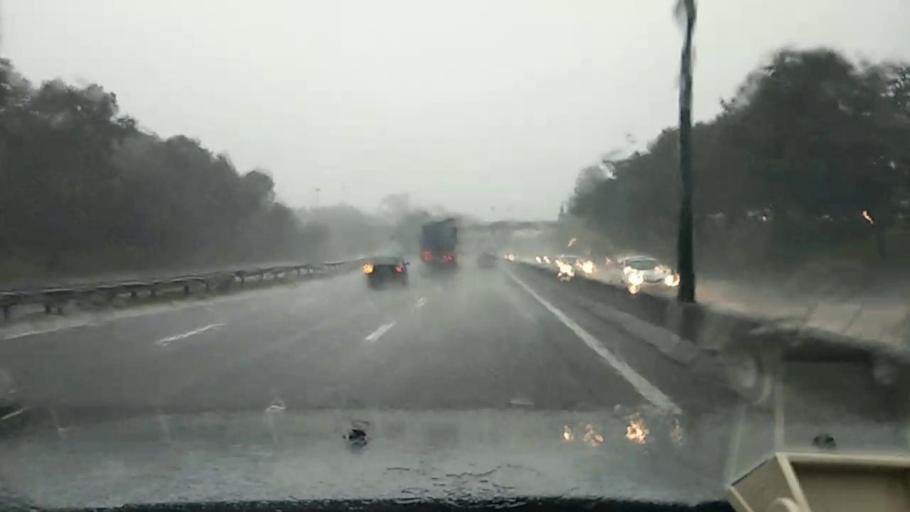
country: MY
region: Selangor
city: Kampong Baharu Balakong
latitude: 2.9818
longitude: 101.7455
